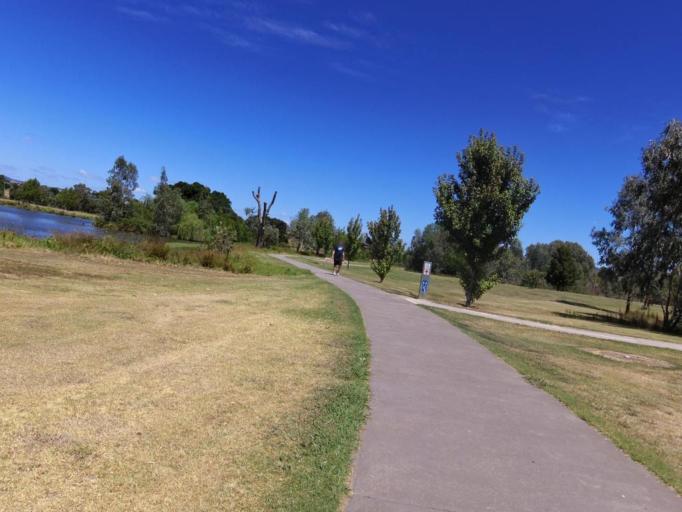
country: AU
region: Victoria
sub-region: Wodonga
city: Wodonga
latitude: -36.1127
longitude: 146.8880
